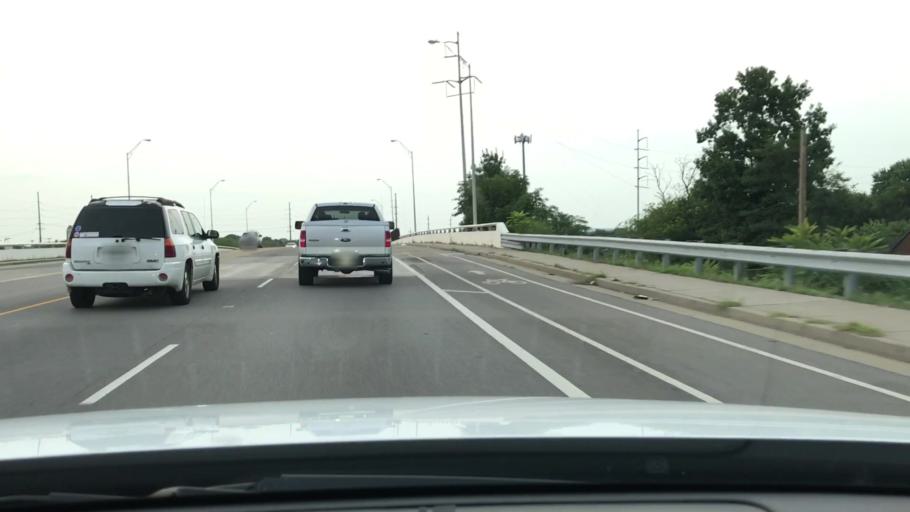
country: US
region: Tennessee
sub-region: Davidson County
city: Goodlettsville
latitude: 36.2749
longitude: -86.7098
